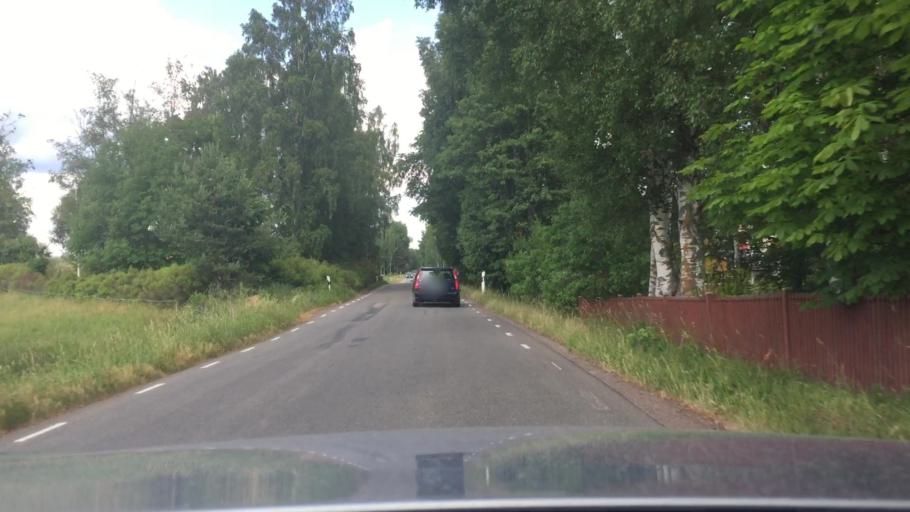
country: SE
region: Vaestra Goetaland
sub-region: Tidaholms Kommun
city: Tidaholm
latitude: 58.1949
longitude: 13.9780
